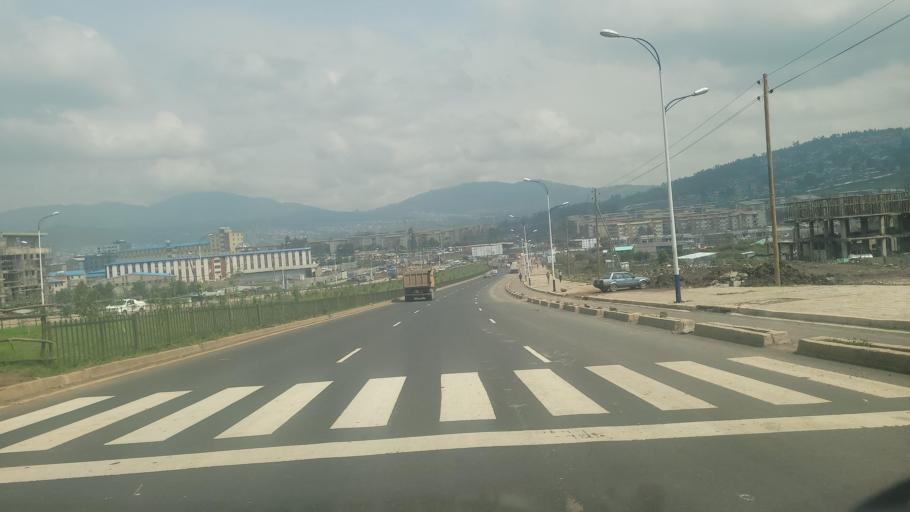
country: ET
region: Adis Abeba
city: Addis Ababa
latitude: 8.9517
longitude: 38.7003
